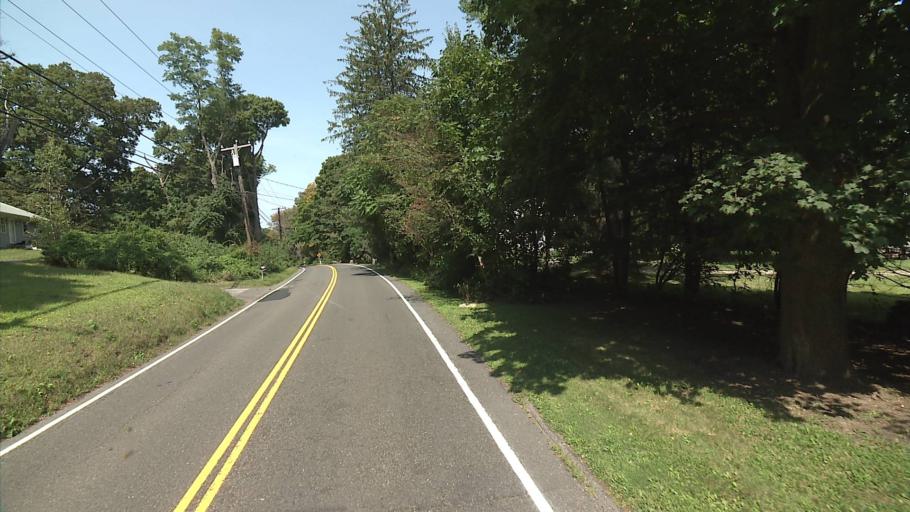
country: US
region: Connecticut
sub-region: Fairfield County
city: Bethel
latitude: 41.3038
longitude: -73.3463
